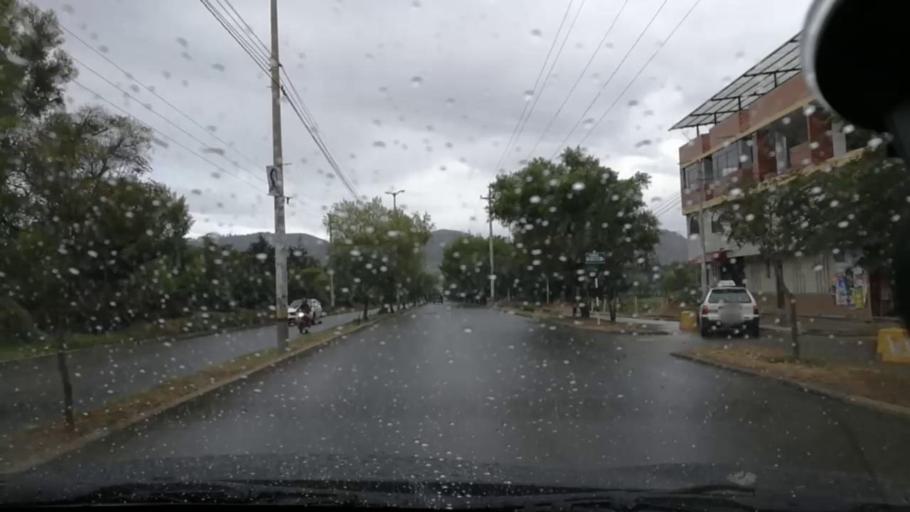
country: PE
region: Cajamarca
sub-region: Provincia de Cajamarca
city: Cajamarca
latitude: -7.1653
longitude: -78.4884
